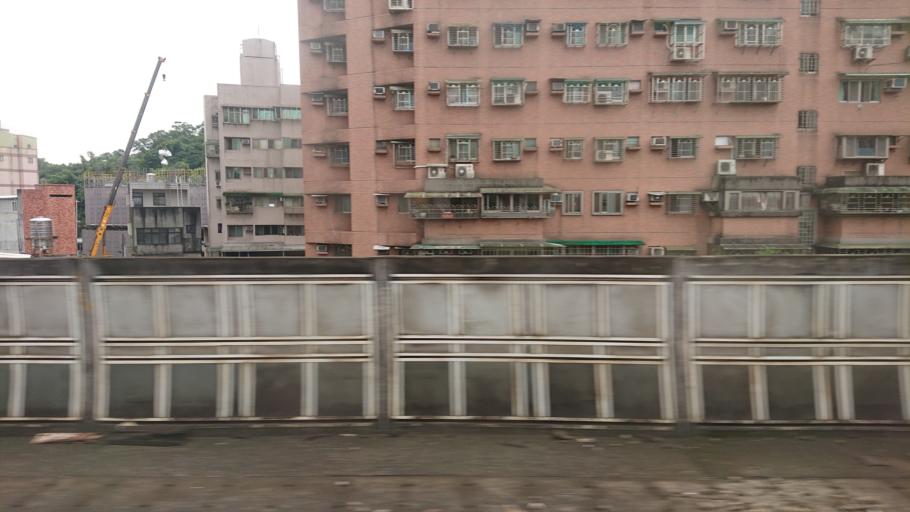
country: TW
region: Taiwan
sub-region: Keelung
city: Keelung
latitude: 25.0747
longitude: 121.6657
